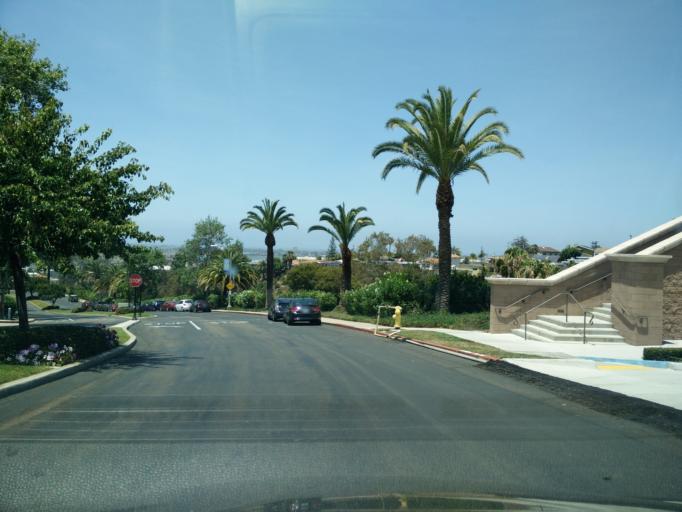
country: US
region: California
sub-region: San Diego County
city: San Diego
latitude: 32.7710
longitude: -117.1943
